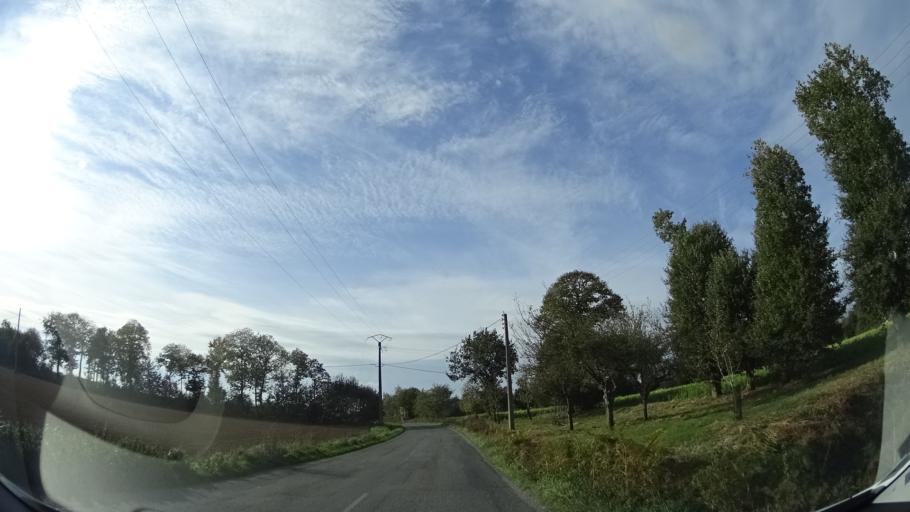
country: FR
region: Brittany
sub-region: Departement d'Ille-et-Vilaine
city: Romille
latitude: 48.2148
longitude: -1.9085
